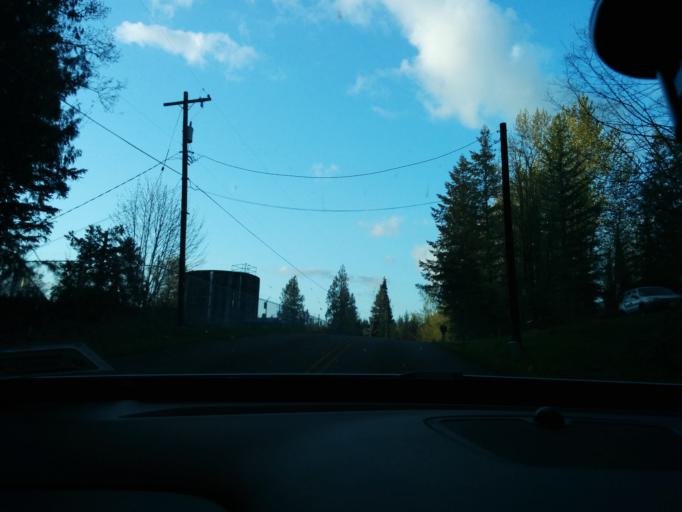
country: US
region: Washington
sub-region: Snohomish County
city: Gold Bar
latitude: 47.8702
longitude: -121.7324
